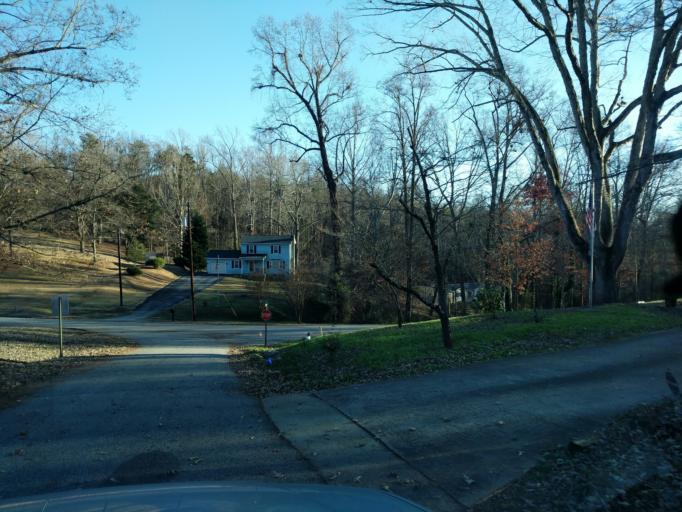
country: US
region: South Carolina
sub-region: Spartanburg County
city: Lyman
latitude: 34.9208
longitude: -82.1208
